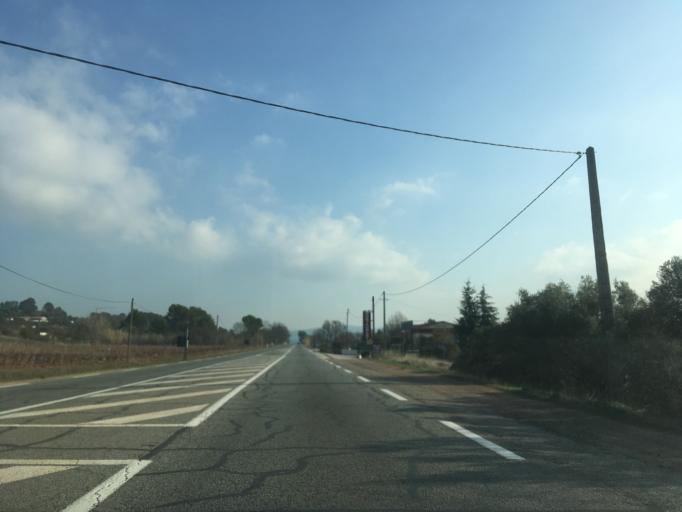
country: FR
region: Provence-Alpes-Cote d'Azur
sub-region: Departement du Var
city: Vidauban
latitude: 43.4043
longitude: 6.3988
